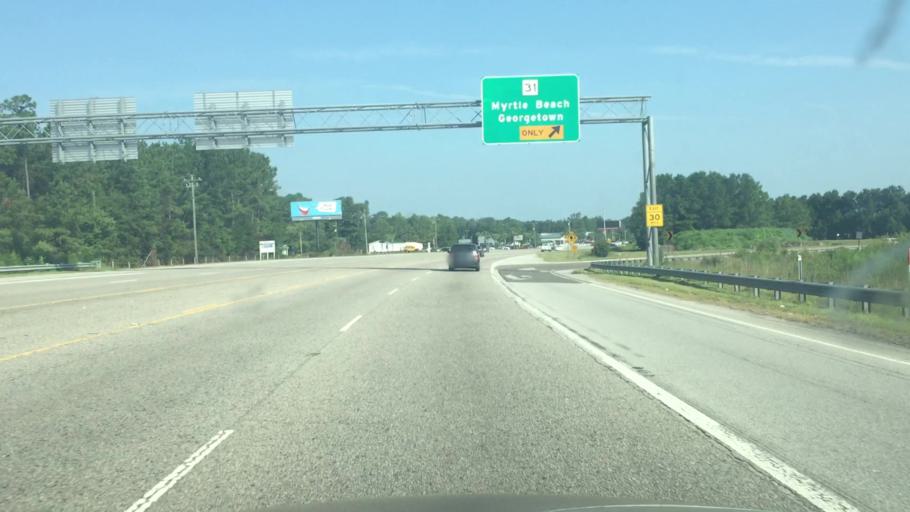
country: US
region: South Carolina
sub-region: Horry County
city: North Myrtle Beach
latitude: 33.8768
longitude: -78.6839
